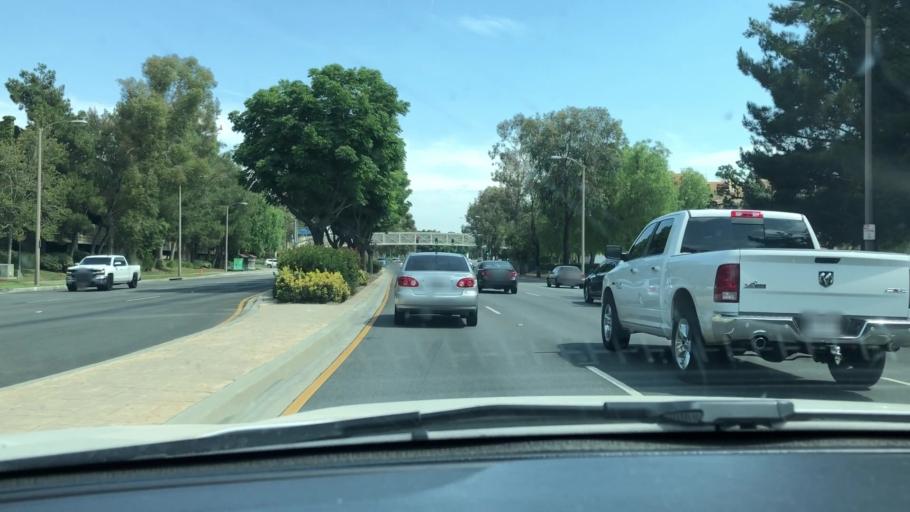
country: US
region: California
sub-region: Los Angeles County
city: Santa Clarita
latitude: 34.4171
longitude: -118.5620
